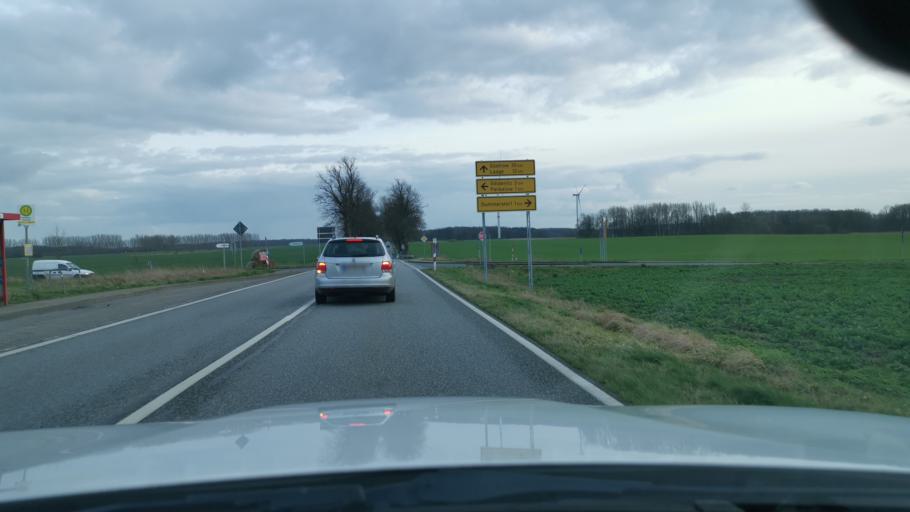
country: DE
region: Mecklenburg-Vorpommern
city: Dummerstorf
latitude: 54.0167
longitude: 12.2468
